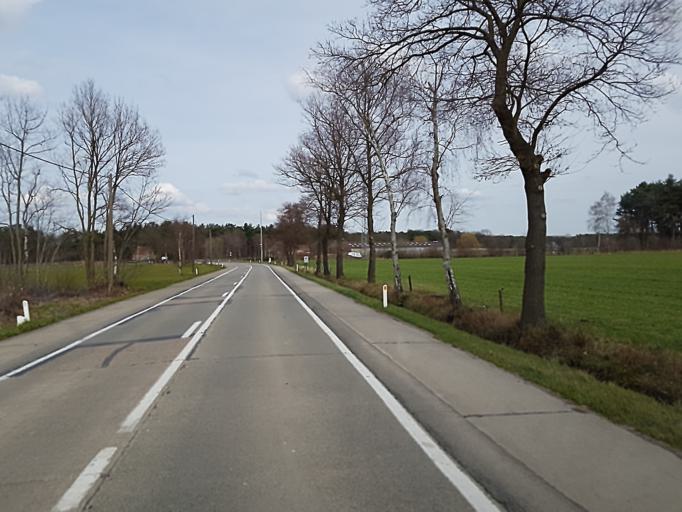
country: BE
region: Flanders
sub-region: Provincie Antwerpen
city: Mol
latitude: 51.1632
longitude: 5.1043
